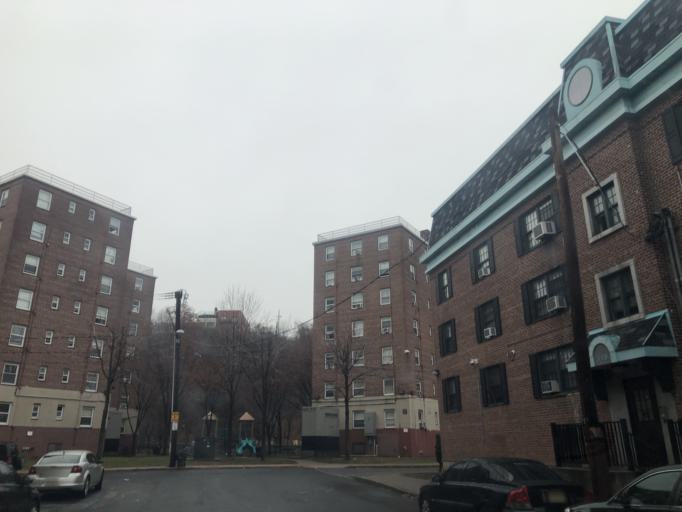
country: US
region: New Jersey
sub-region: Hudson County
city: Hoboken
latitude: 40.7426
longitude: -74.0412
